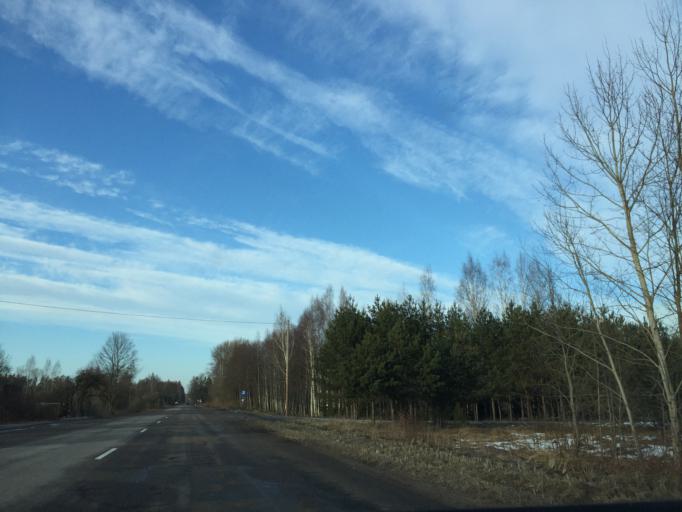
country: LV
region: Kekava
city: Balozi
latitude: 56.7320
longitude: 24.1097
